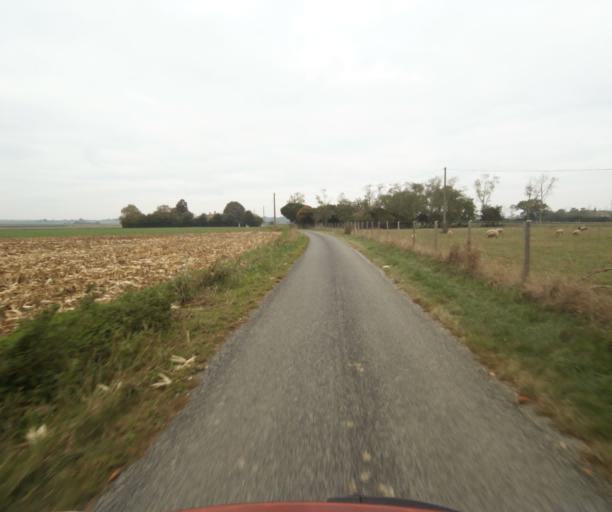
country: FR
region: Midi-Pyrenees
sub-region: Departement du Tarn-et-Garonne
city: Verdun-sur-Garonne
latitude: 43.8128
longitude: 1.2330
